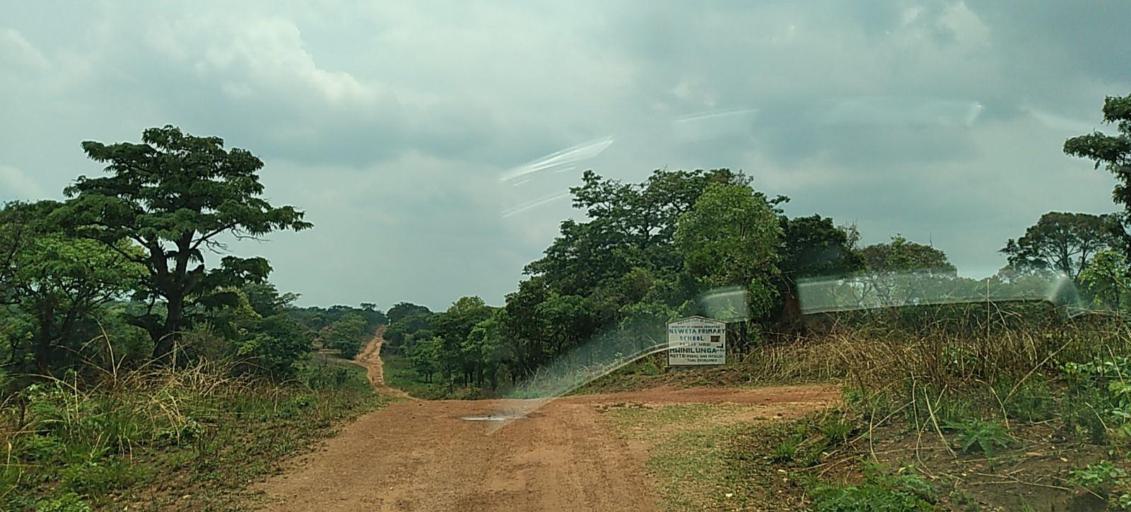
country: ZM
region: North-Western
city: Mwinilunga
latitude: -11.5380
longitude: 24.7827
